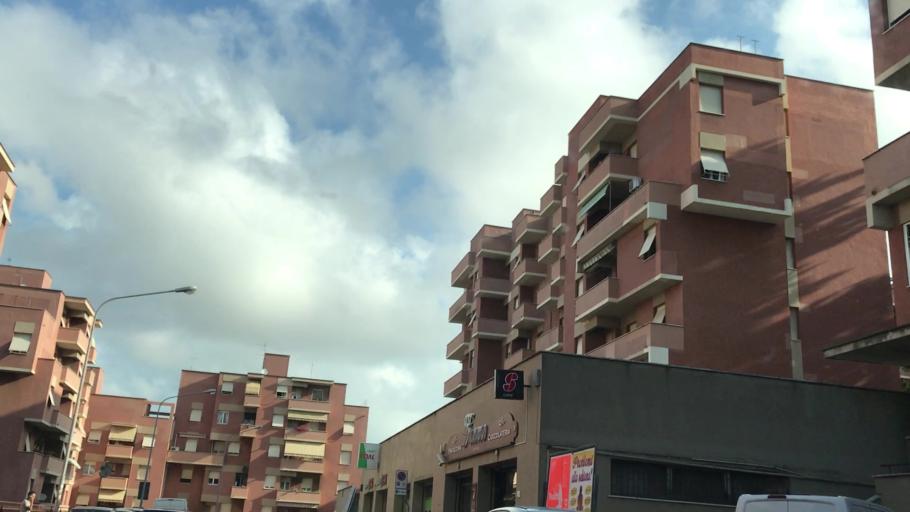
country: IT
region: The Marches
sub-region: Provincia di Ancona
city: Le Grazie di Ancona
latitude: 43.5930
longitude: 13.5143
